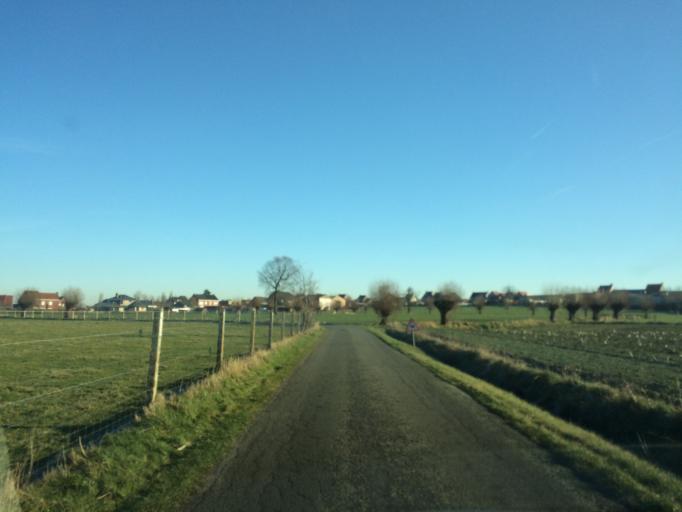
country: BE
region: Flanders
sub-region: Provincie West-Vlaanderen
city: Jabbeke
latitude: 51.1236
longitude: 3.0802
